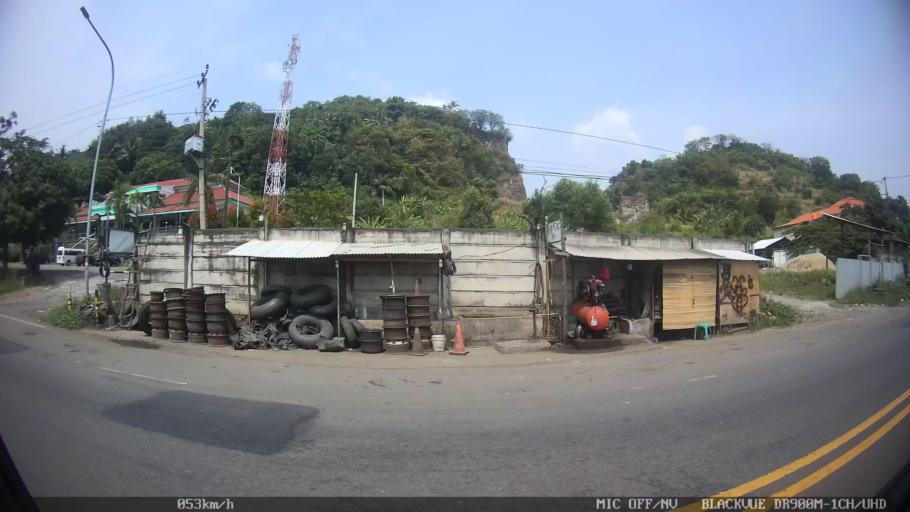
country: ID
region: Banten
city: Curug
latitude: -5.9521
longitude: 106.0016
